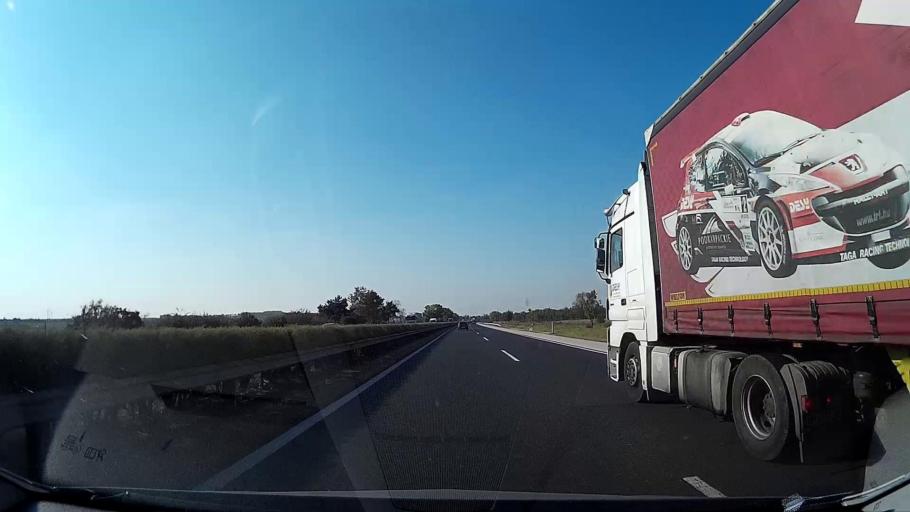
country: HU
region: Komarom-Esztergom
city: Mocsa
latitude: 47.6450
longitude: 18.2108
